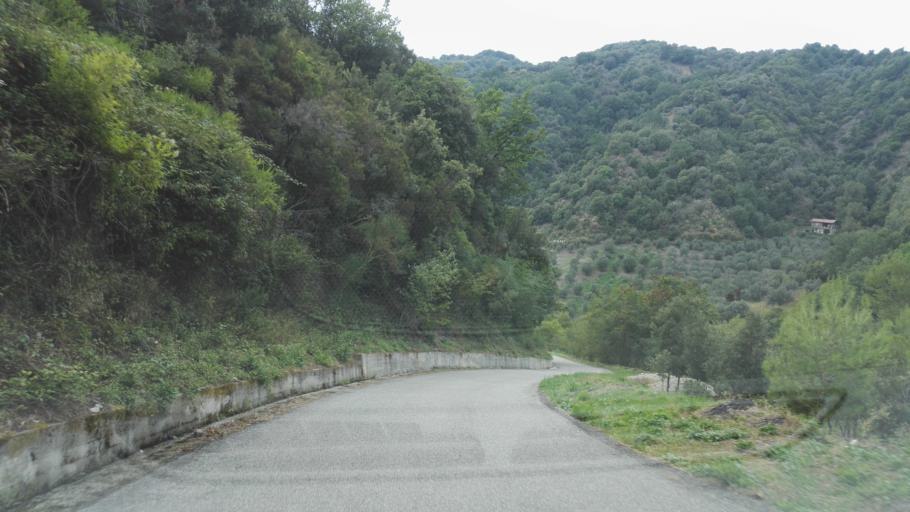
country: IT
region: Calabria
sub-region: Provincia di Reggio Calabria
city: Caulonia
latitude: 38.4344
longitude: 16.4014
